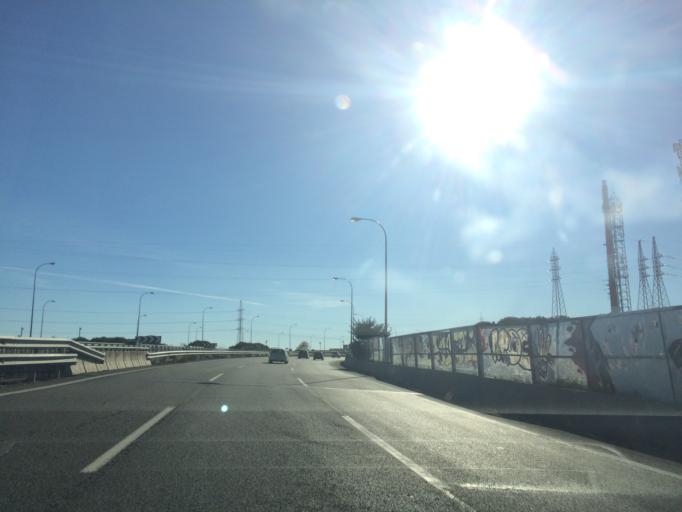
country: ES
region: Madrid
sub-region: Provincia de Madrid
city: Pozuelo de Alarcon
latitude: 40.4118
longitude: -3.8217
